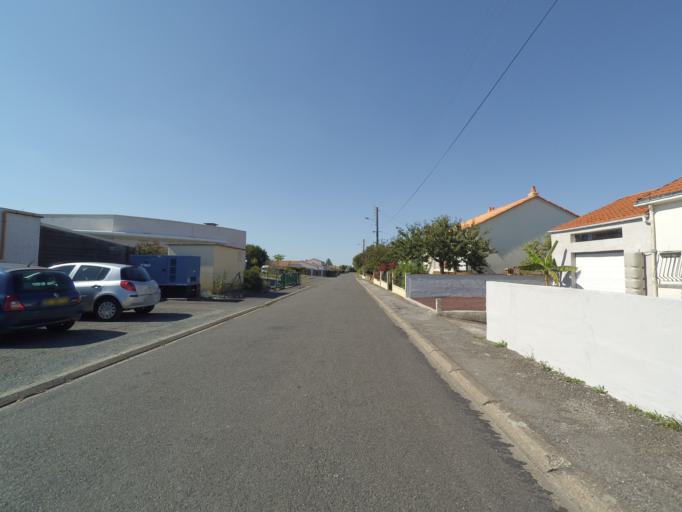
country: FR
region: Pays de la Loire
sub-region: Departement de la Loire-Atlantique
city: Vieillevigne
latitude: 46.9672
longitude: -1.4419
